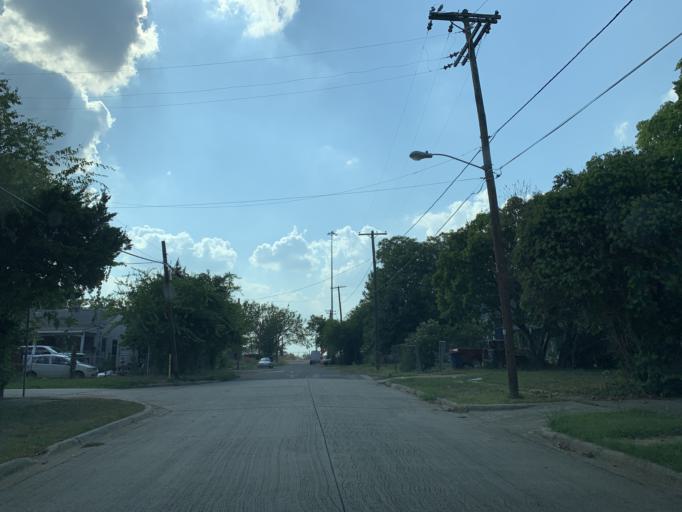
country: US
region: Texas
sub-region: Dallas County
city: Dallas
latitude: 32.7468
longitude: -96.8081
